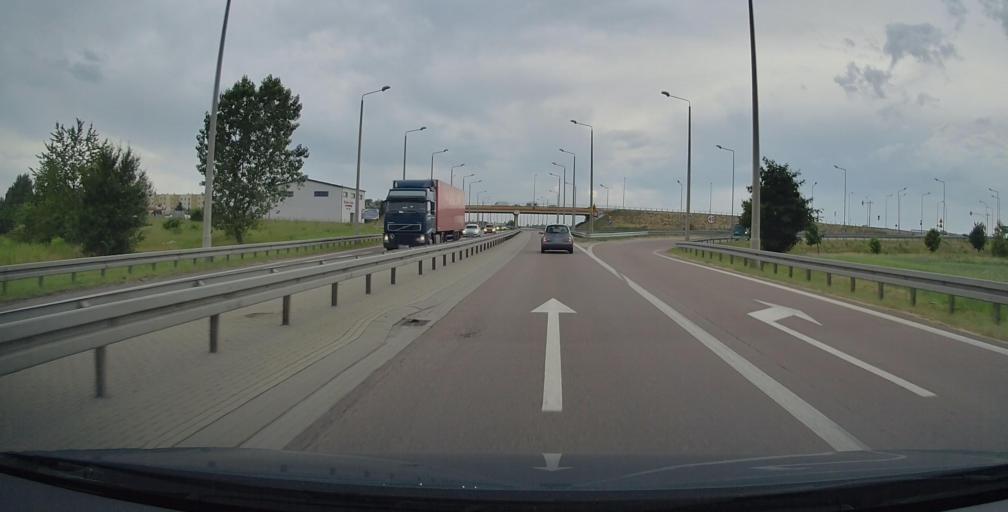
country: PL
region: Lublin Voivodeship
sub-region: Biala Podlaska
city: Biala Podlaska
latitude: 52.0526
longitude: 23.1230
